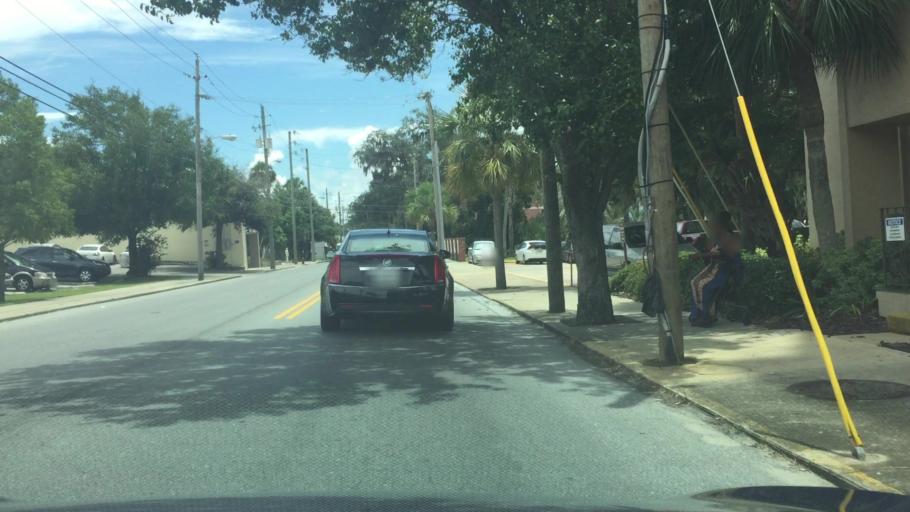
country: US
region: Florida
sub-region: Bay County
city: Panama City
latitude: 30.1535
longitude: -85.6619
